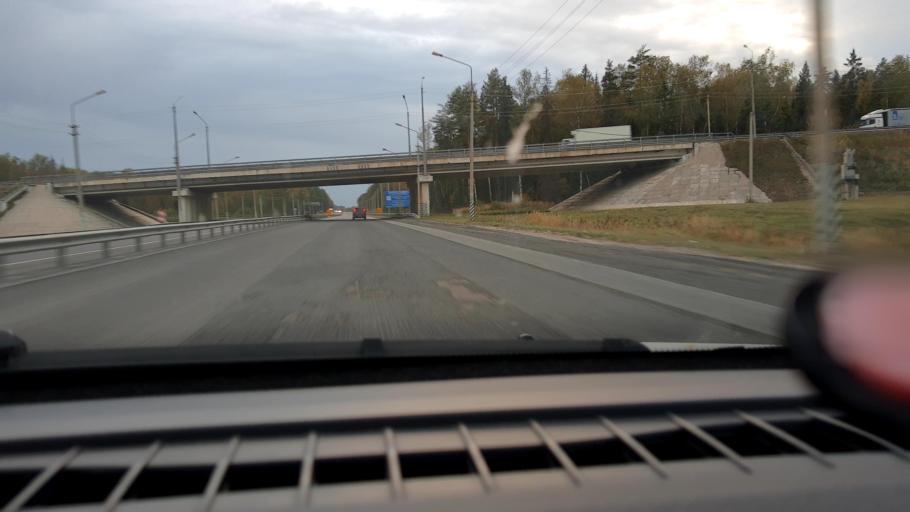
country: RU
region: Vladimir
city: Kameshkovo
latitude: 56.1944
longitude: 40.9534
